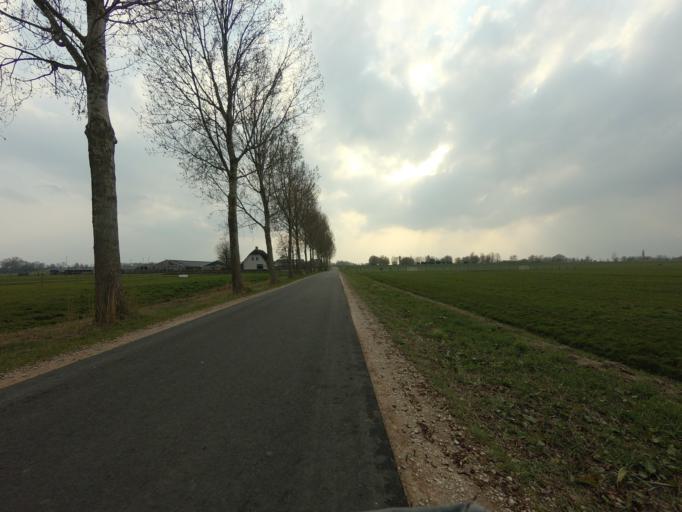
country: NL
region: Utrecht
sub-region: Gemeente De Ronde Venen
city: Mijdrecht
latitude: 52.1907
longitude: 4.8404
